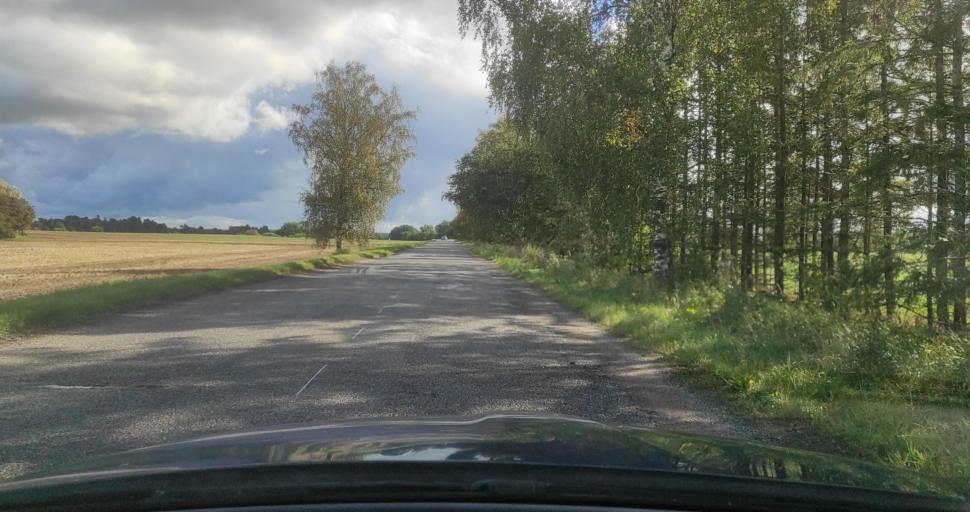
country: LV
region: Ventspils Rajons
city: Piltene
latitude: 57.2631
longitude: 21.6002
